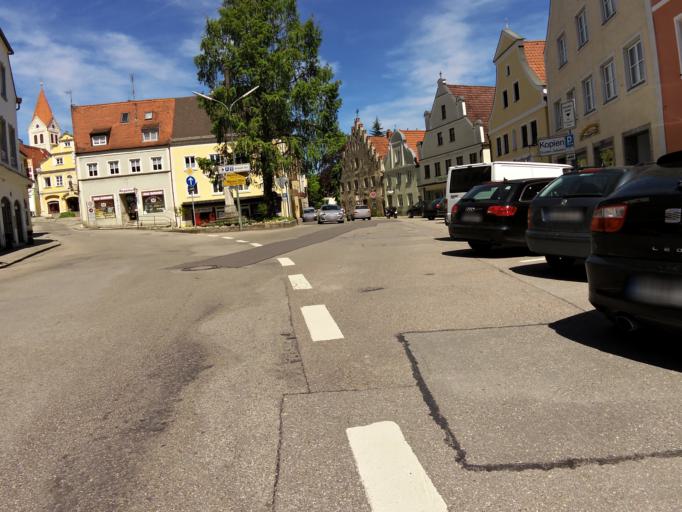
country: DE
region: Bavaria
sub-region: Upper Bavaria
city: Moosburg
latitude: 48.4674
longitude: 11.9382
